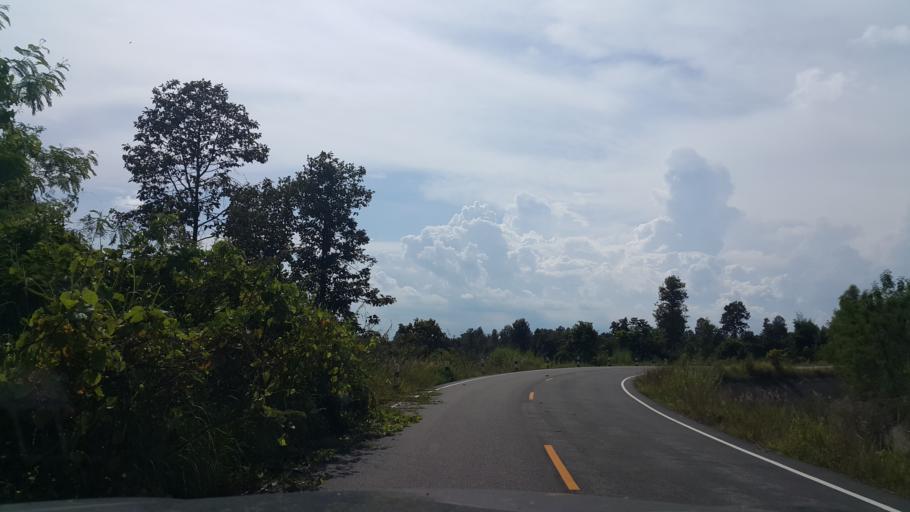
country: TH
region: Chiang Mai
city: Mae On
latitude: 18.8081
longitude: 99.1943
